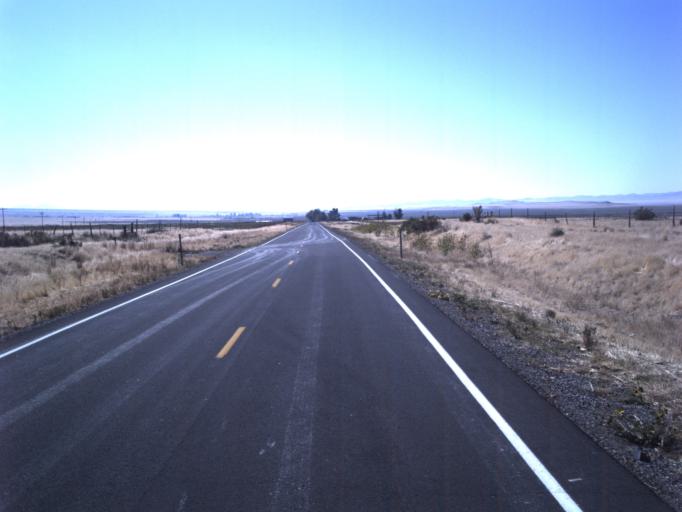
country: US
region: Utah
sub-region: Tooele County
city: Grantsville
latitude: 40.5072
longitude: -112.7480
